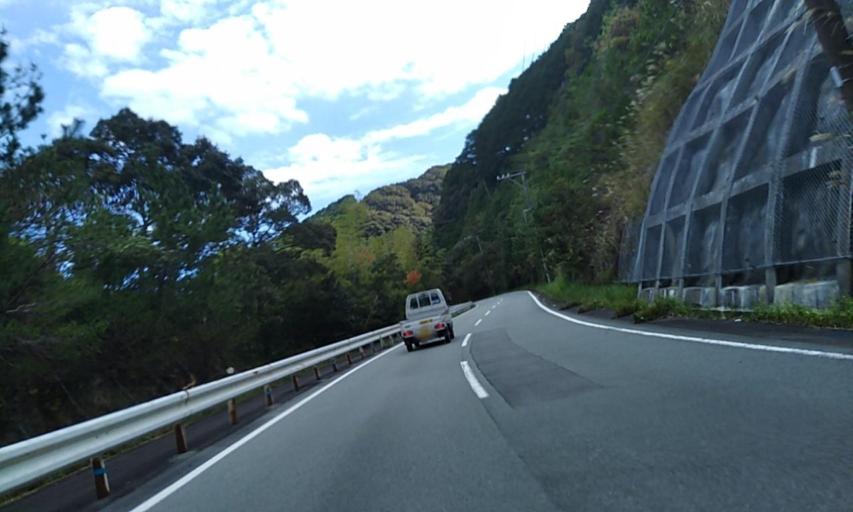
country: JP
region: Mie
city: Ise
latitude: 34.2957
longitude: 136.5983
